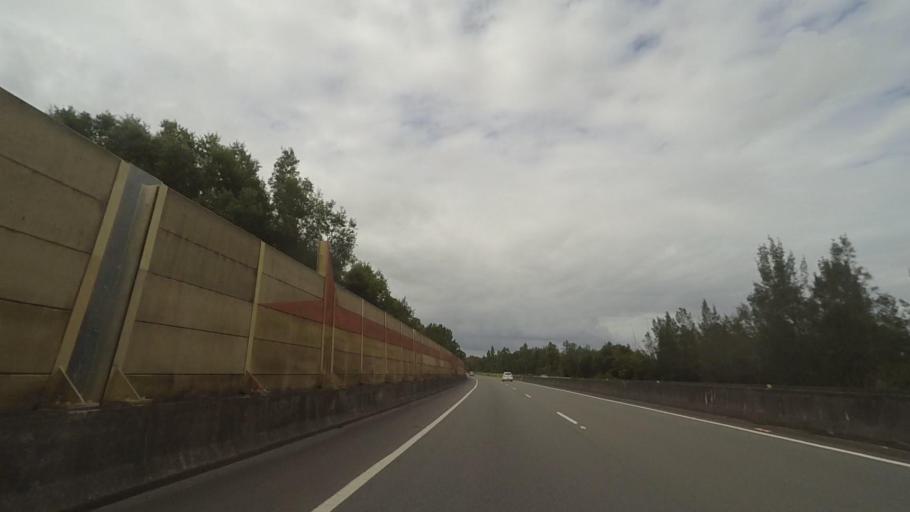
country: AU
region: New South Wales
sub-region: Port Stephens Shire
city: Raymond Terrace
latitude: -32.7694
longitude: 151.7617
